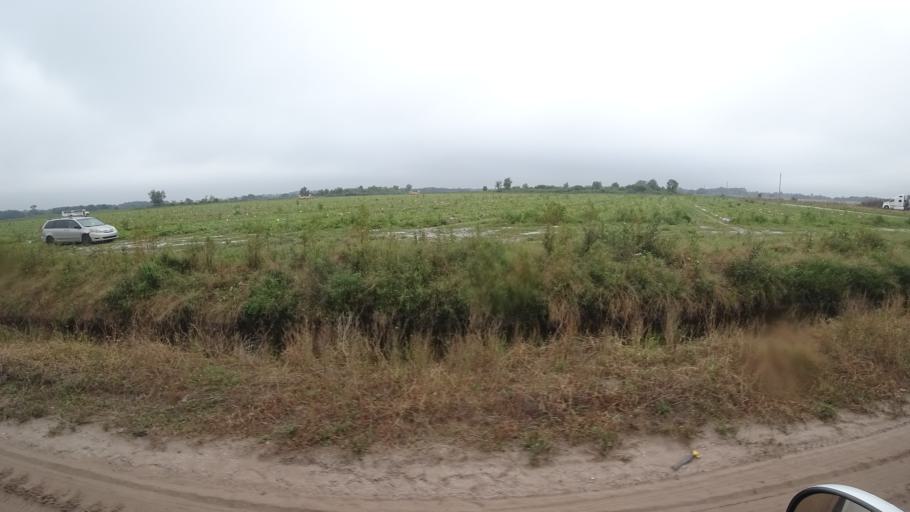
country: US
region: Florida
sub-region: Sarasota County
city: Warm Mineral Springs
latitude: 27.2804
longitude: -82.1695
